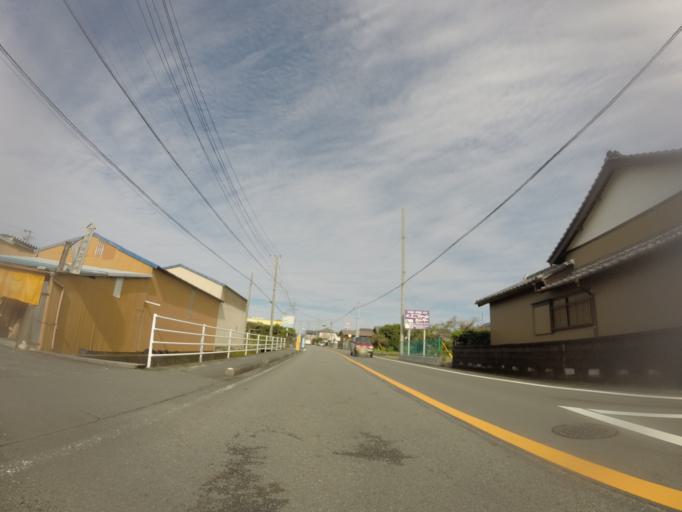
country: JP
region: Shizuoka
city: Shimada
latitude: 34.7758
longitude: 138.2515
